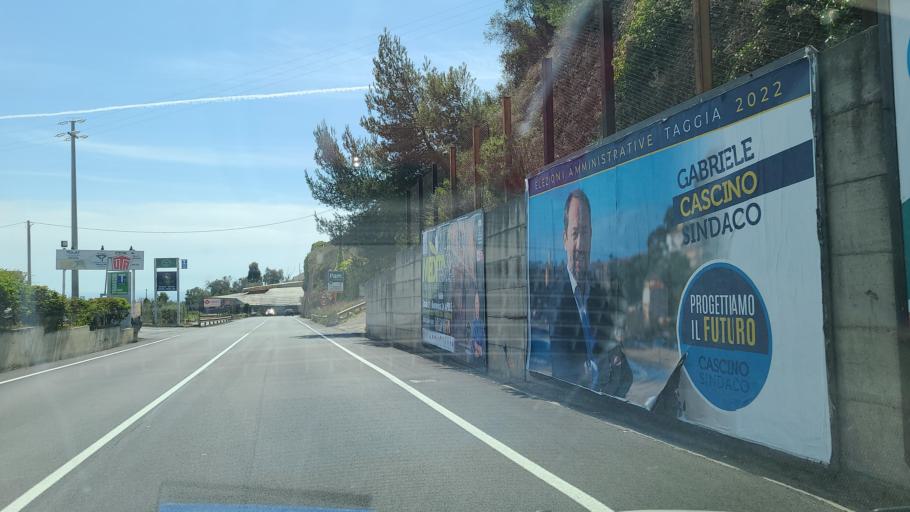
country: IT
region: Liguria
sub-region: Provincia di Imperia
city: Taggia
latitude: 43.8474
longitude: 7.8409
